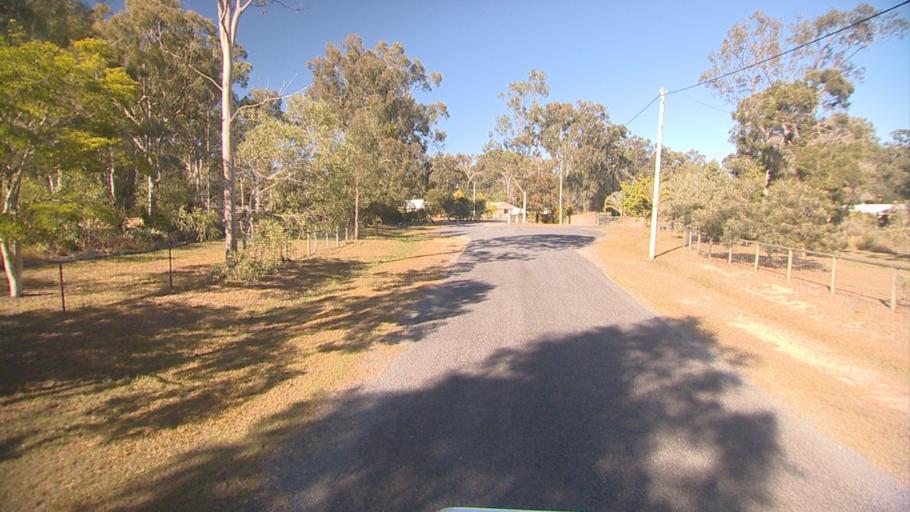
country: AU
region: Queensland
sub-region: Logan
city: Chambers Flat
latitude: -27.7866
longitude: 153.1259
